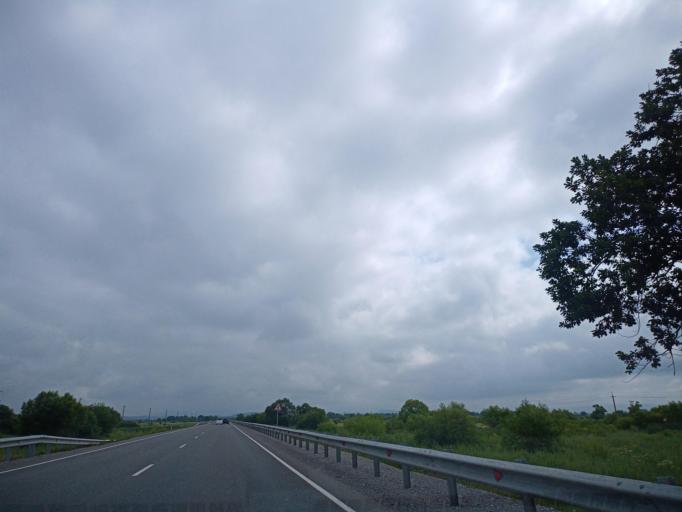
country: RU
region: Primorskiy
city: Dal'nerechensk
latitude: 45.9778
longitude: 133.7963
